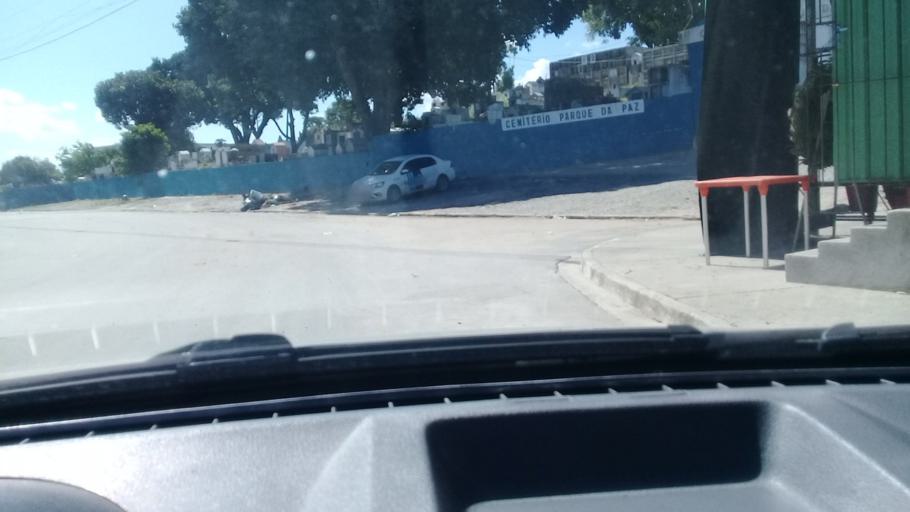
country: BR
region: Pernambuco
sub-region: Jaboatao Dos Guararapes
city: Jaboatao
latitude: -8.1534
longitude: -34.9496
